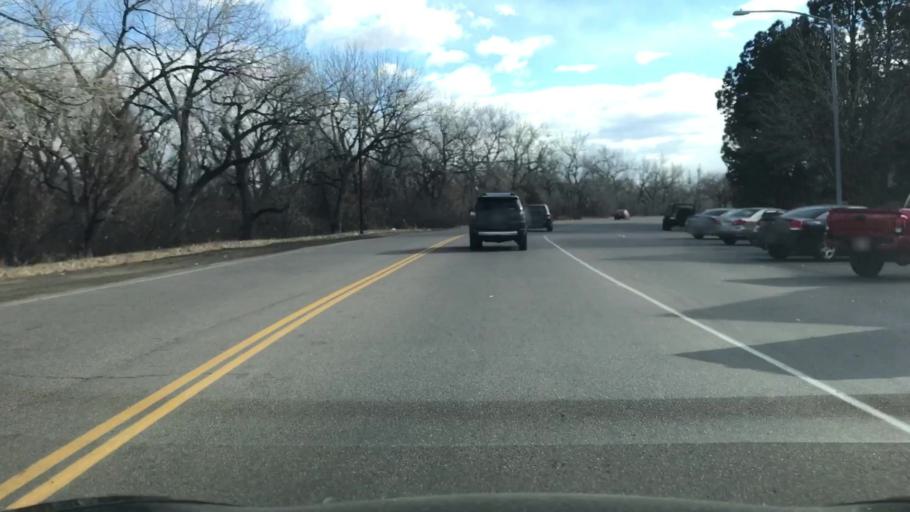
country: US
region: Colorado
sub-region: Arapahoe County
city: Glendale
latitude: 39.7029
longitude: -104.9305
